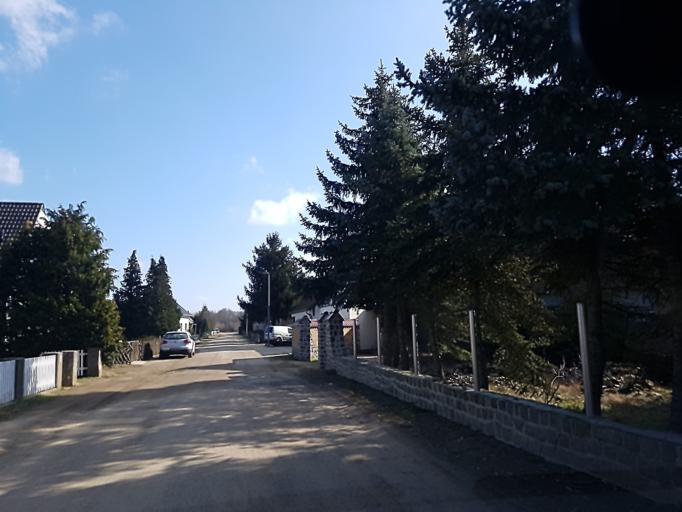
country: DE
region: Brandenburg
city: Doberlug-Kirchhain
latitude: 51.6037
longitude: 13.5550
